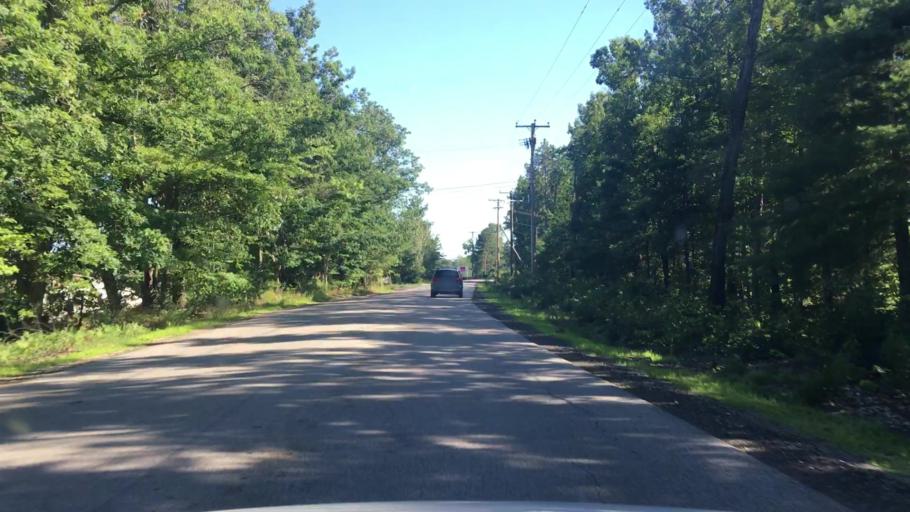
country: US
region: New Hampshire
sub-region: Rockingham County
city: Brentwood
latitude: 43.0048
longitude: -71.0136
